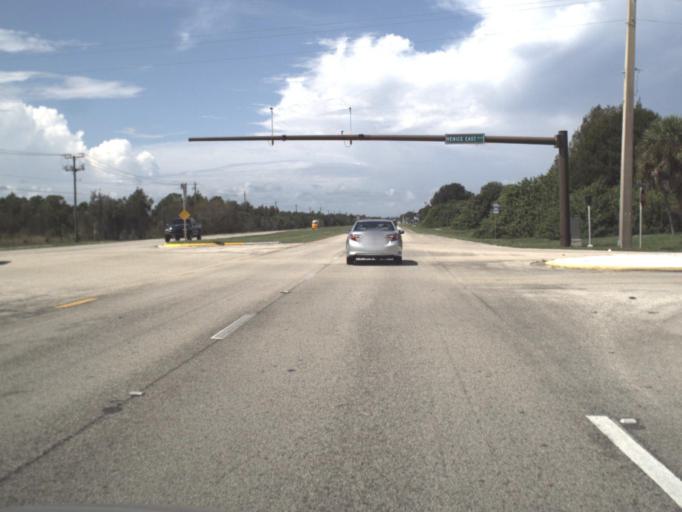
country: US
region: Florida
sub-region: Sarasota County
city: Plantation
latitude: 27.0498
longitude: -82.3772
